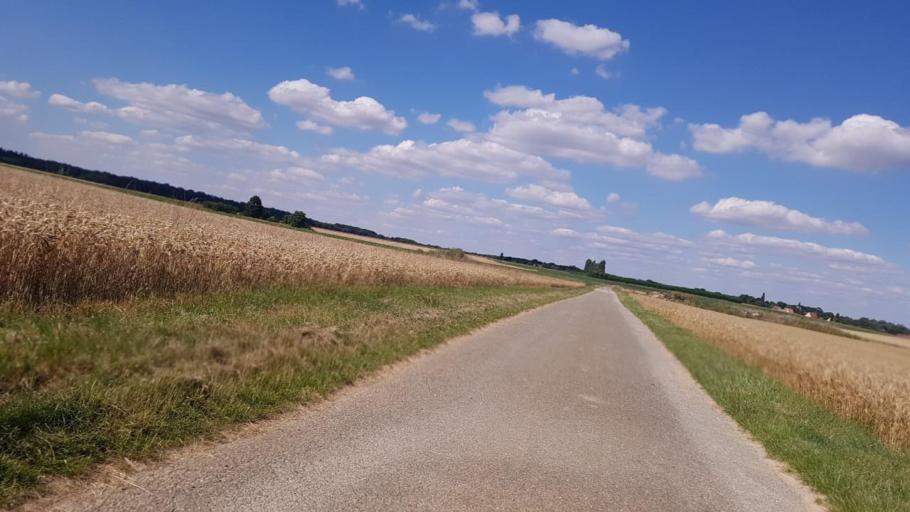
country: FR
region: Picardie
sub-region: Departement de l'Oise
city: Ver-sur-Launette
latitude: 49.0958
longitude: 2.6743
